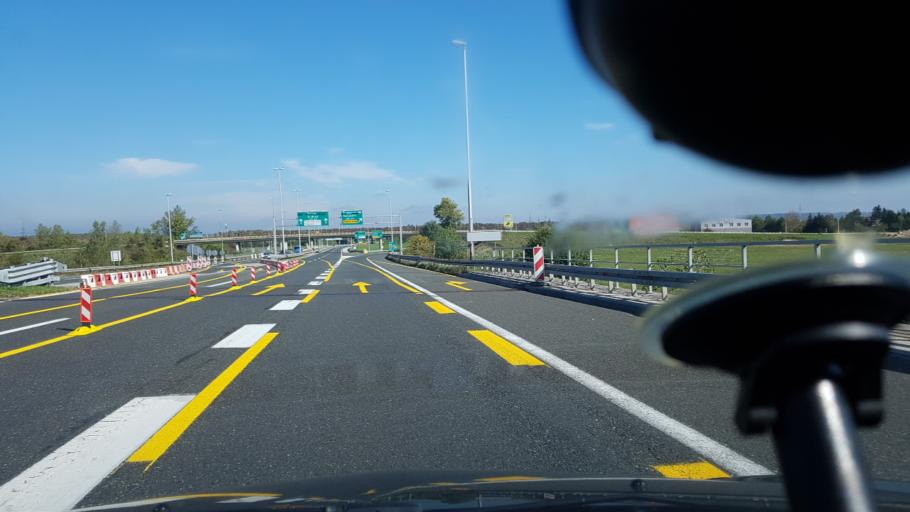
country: HR
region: Grad Zagreb
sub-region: Sesvete
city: Sesvete
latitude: 45.7902
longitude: 16.1263
